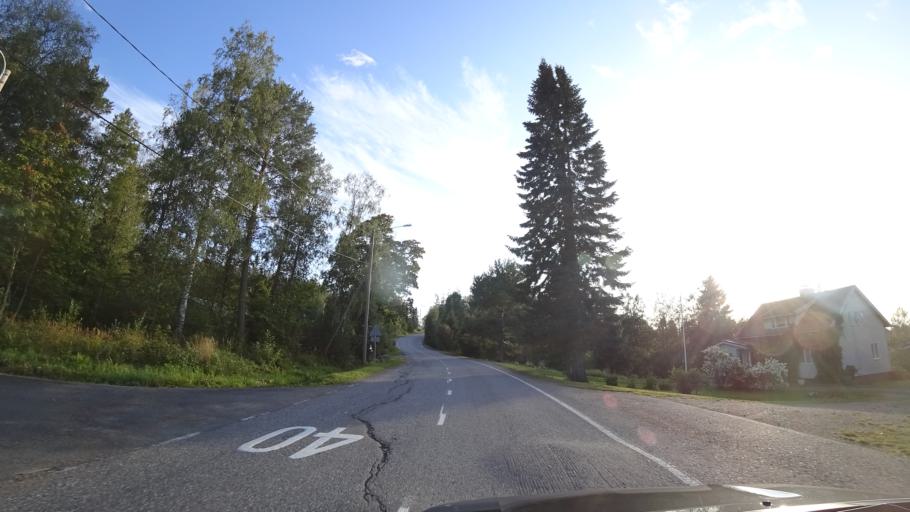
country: FI
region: Haeme
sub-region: Haemeenlinna
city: Lammi
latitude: 61.0708
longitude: 25.0083
